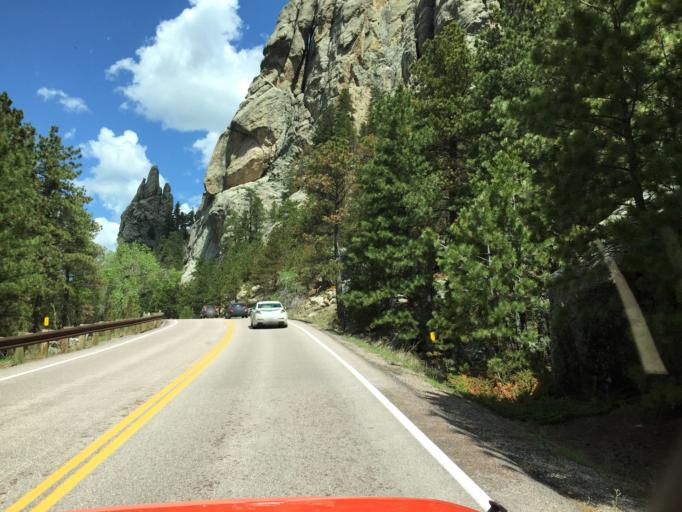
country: US
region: South Dakota
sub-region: Custer County
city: Custer
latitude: 43.8773
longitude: -103.4604
